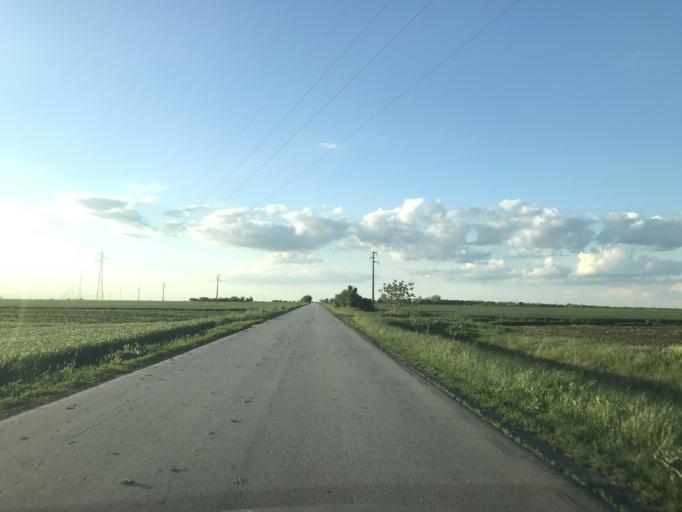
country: RS
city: Mihajlovo
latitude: 45.4377
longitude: 20.3915
